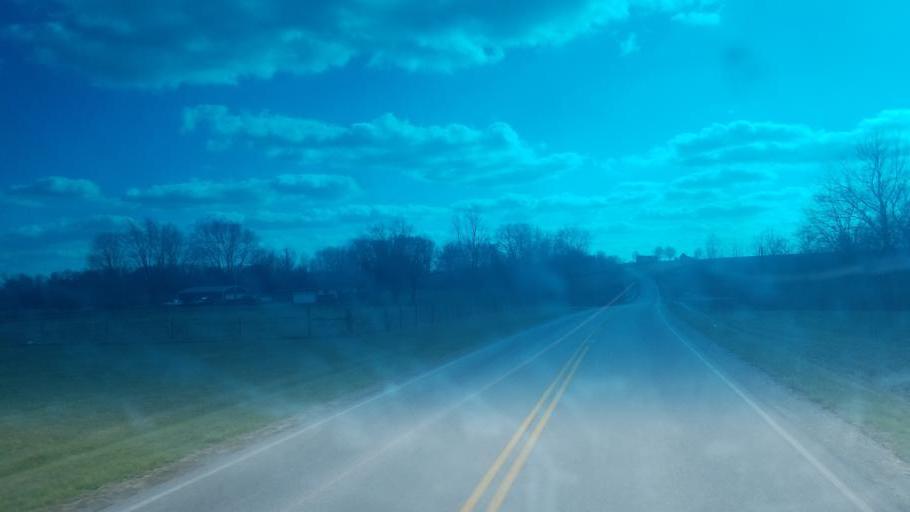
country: US
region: Ohio
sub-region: Highland County
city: Greenfield
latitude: 39.3109
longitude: -83.4328
